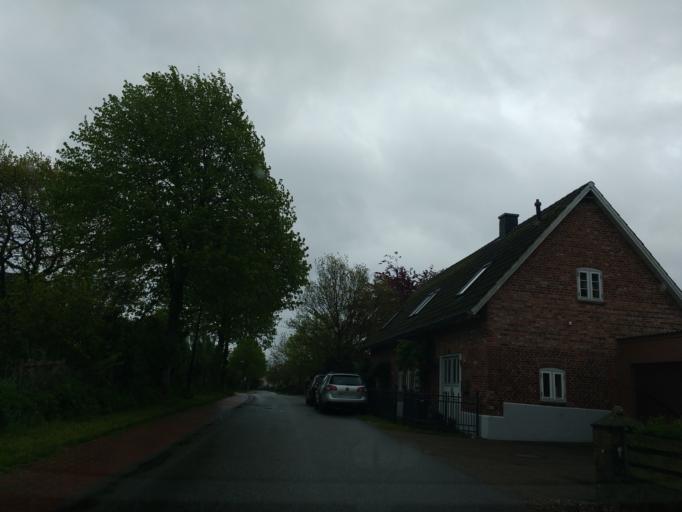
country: DE
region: Schleswig-Holstein
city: Waabs
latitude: 54.5167
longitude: 9.9788
